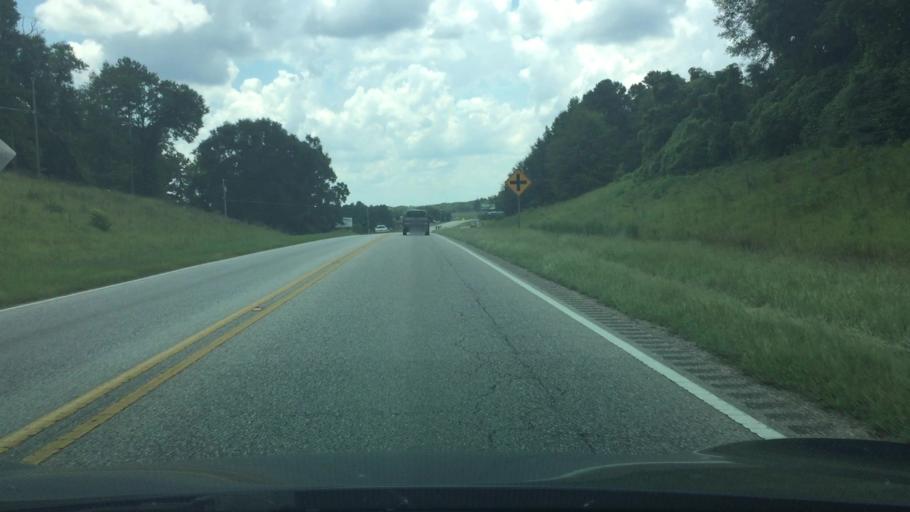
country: US
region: Alabama
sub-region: Pike County
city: Troy
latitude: 31.7127
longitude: -85.9592
